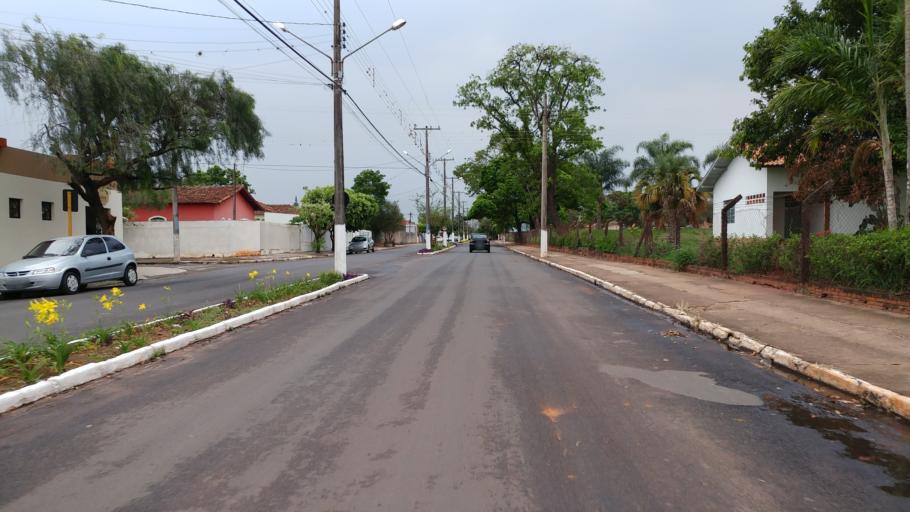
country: BR
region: Sao Paulo
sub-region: Paraguacu Paulista
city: Paraguacu Paulista
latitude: -22.4164
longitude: -50.5842
